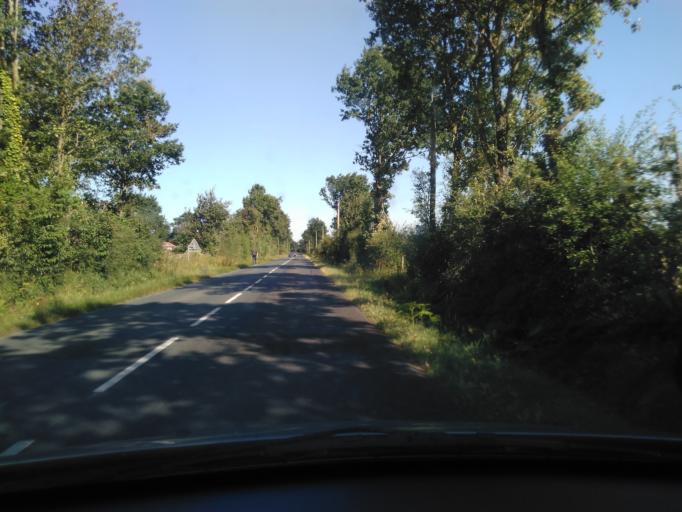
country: FR
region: Pays de la Loire
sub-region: Departement de la Vendee
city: Dompierre-sur-Yon
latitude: 46.7302
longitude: -1.3646
